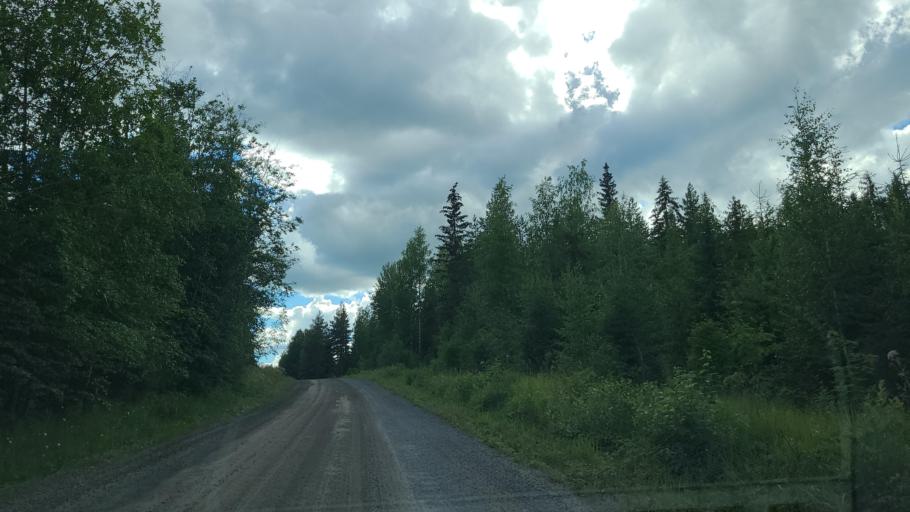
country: FI
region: Central Finland
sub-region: Jaemsae
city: Jaemsae
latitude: 61.9274
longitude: 25.3220
